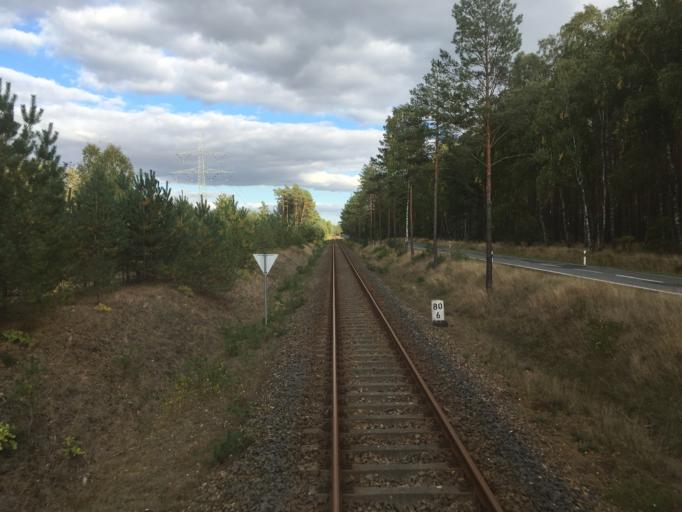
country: DE
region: Mecklenburg-Vorpommern
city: Malchow
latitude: 53.5303
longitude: 12.4755
